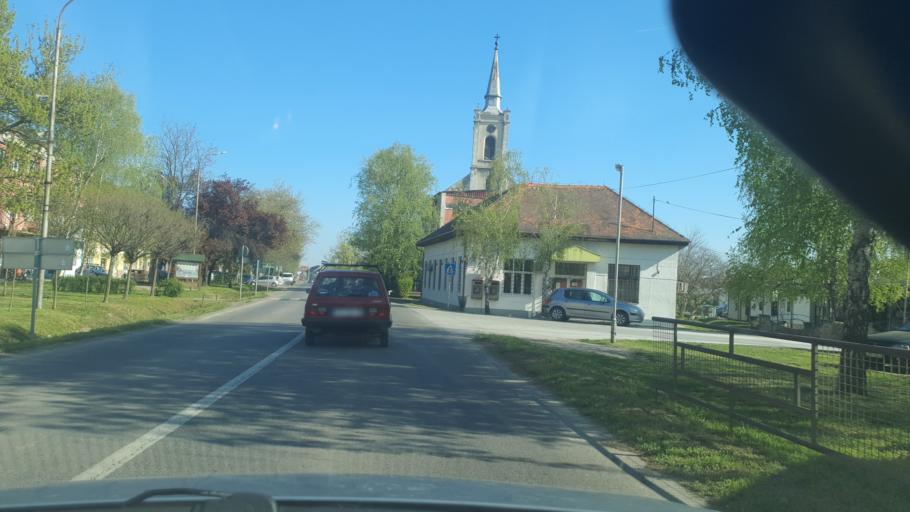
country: RS
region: Autonomna Pokrajina Vojvodina
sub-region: Zapadnobacki Okrug
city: Kula
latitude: 45.7016
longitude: 19.3819
